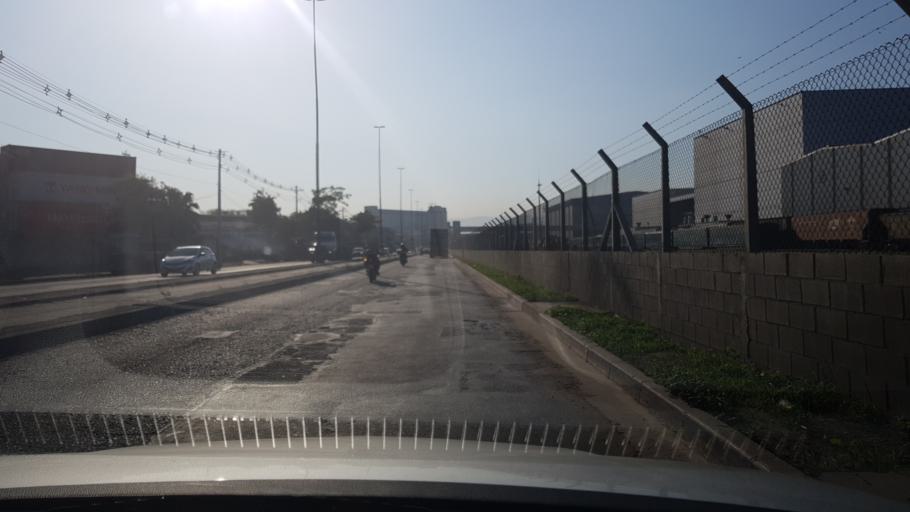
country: BR
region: Sao Paulo
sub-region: Santos
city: Santos
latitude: -23.9653
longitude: -46.3027
